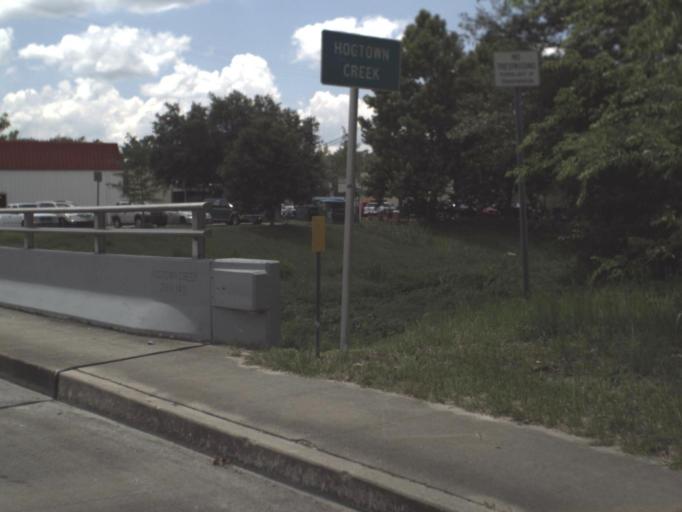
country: US
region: Florida
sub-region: Alachua County
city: Gainesville
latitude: 29.6531
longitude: -82.3725
